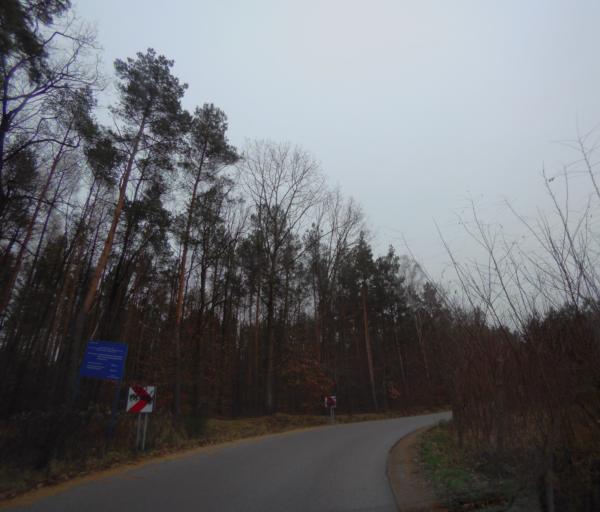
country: PL
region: Subcarpathian Voivodeship
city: Nowa Sarzyna
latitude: 50.3124
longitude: 22.3423
